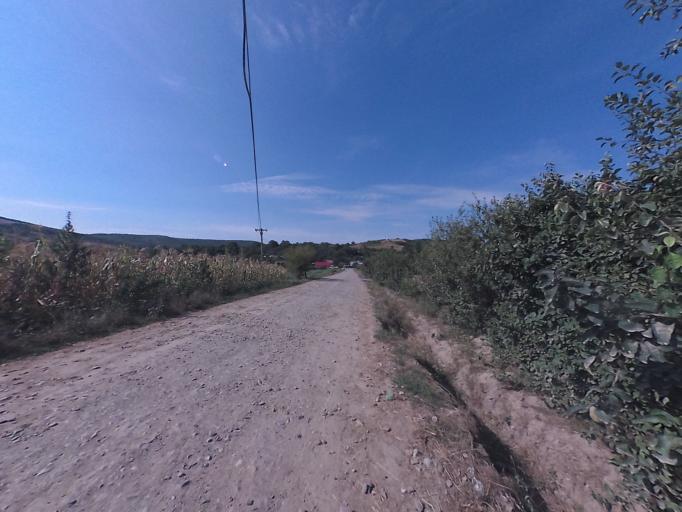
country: RO
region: Vaslui
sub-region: Comuna Osesti
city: Buda
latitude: 46.7614
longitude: 27.4275
